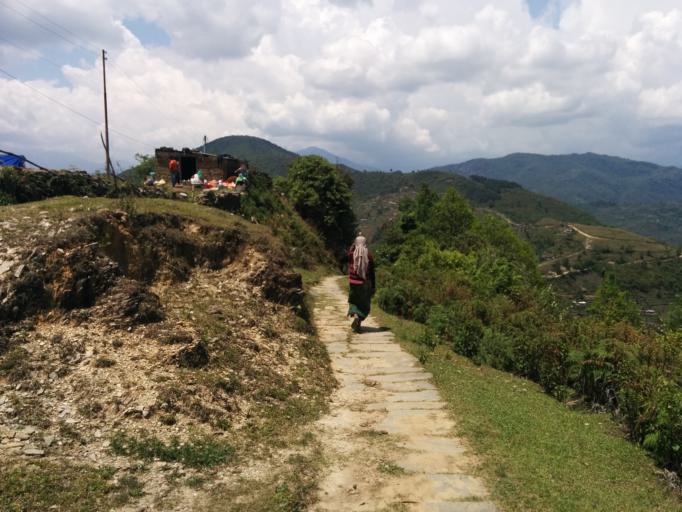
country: NP
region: Western Region
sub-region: Gandaki Zone
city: Pokhara
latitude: 28.2599
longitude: 83.8207
